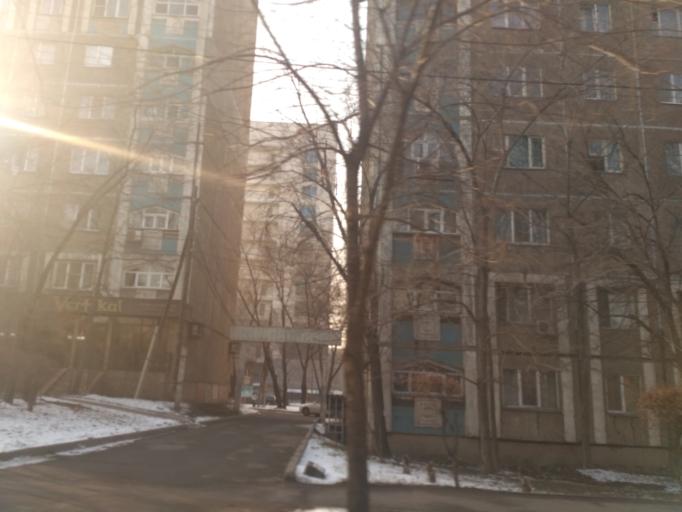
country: KZ
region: Almaty Qalasy
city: Almaty
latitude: 43.2537
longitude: 76.9147
